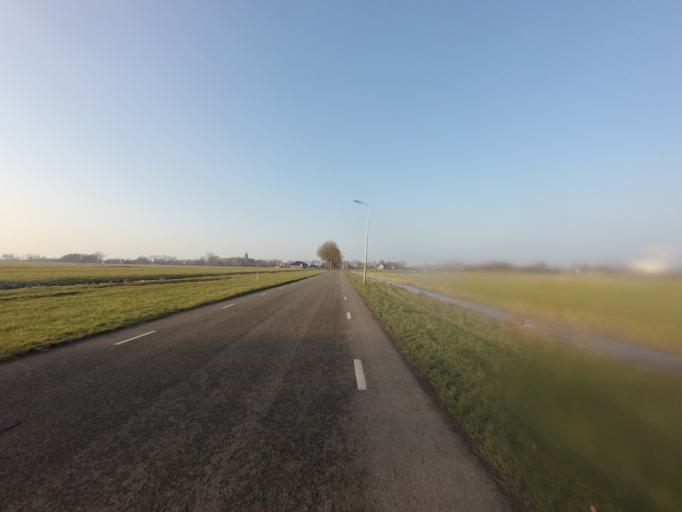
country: NL
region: South Holland
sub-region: Gemeente Vlist
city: Vlist
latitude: 52.0078
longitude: 4.8103
